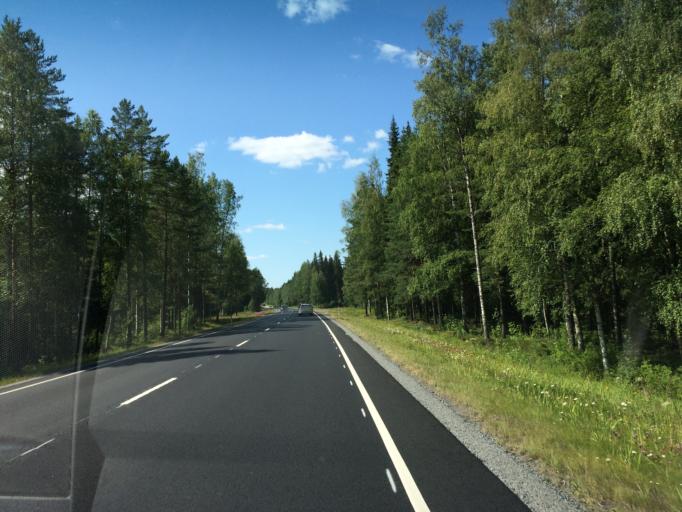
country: FI
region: Pirkanmaa
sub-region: Lounais-Pirkanmaa
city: Kiikoinen
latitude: 61.4757
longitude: 22.4608
